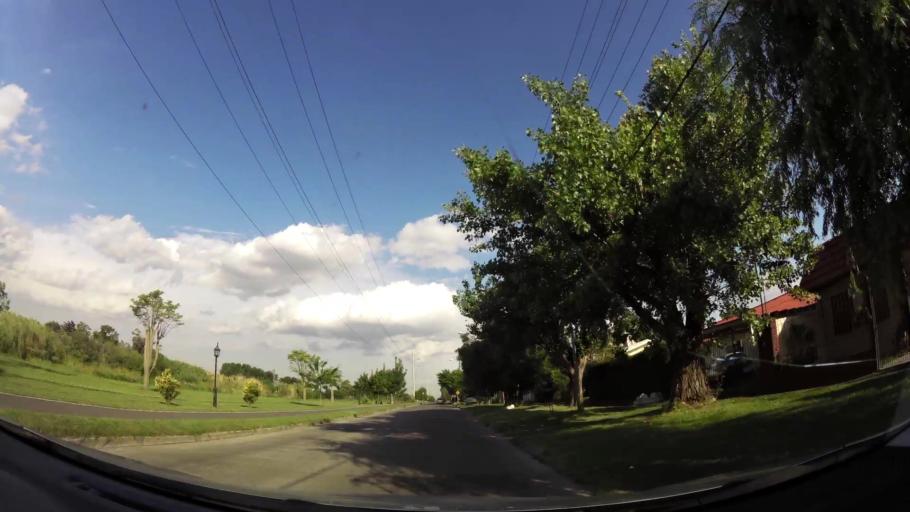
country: AR
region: Buenos Aires
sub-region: Partido de Tigre
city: Tigre
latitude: -34.4661
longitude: -58.6390
